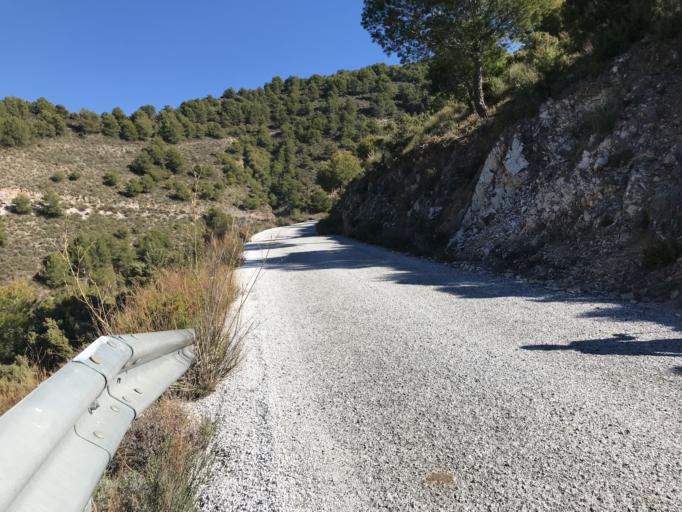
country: ES
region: Andalusia
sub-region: Provincia de Malaga
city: Canillas de Albaida
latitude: 36.8560
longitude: -3.9886
